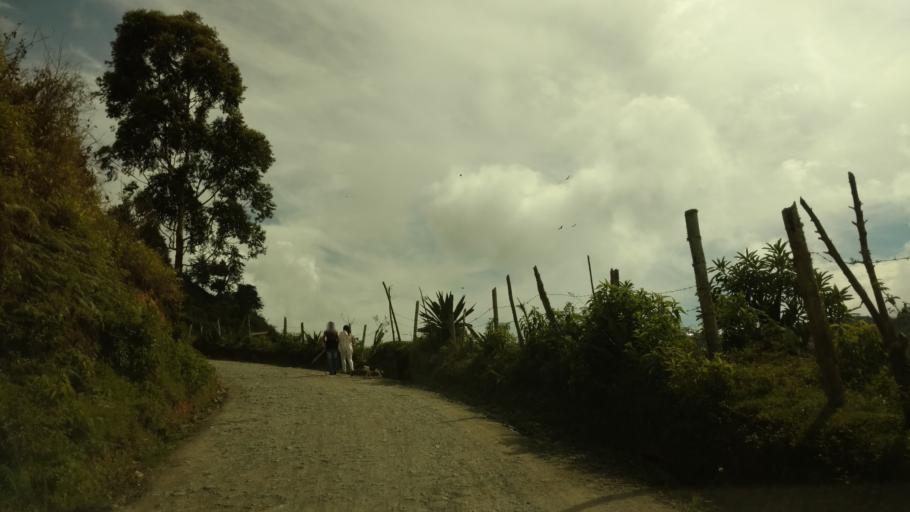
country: CO
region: Caldas
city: Aguadas
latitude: 5.6215
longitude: -75.4537
